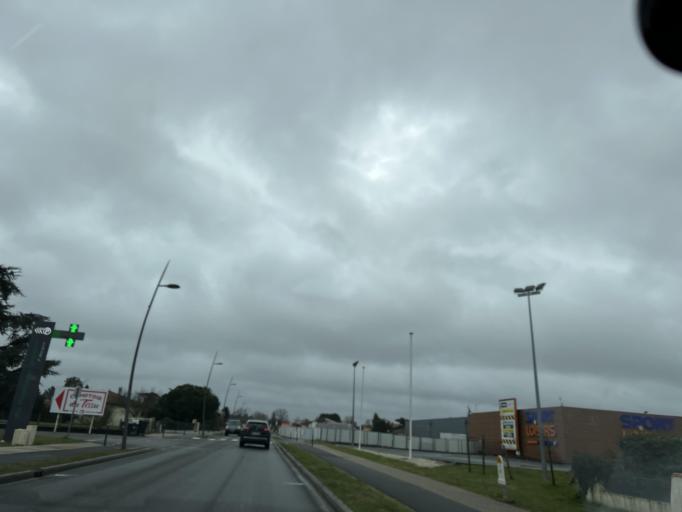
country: FR
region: Aquitaine
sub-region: Departement de la Gironde
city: Lesparre-Medoc
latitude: 45.3022
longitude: -0.9345
